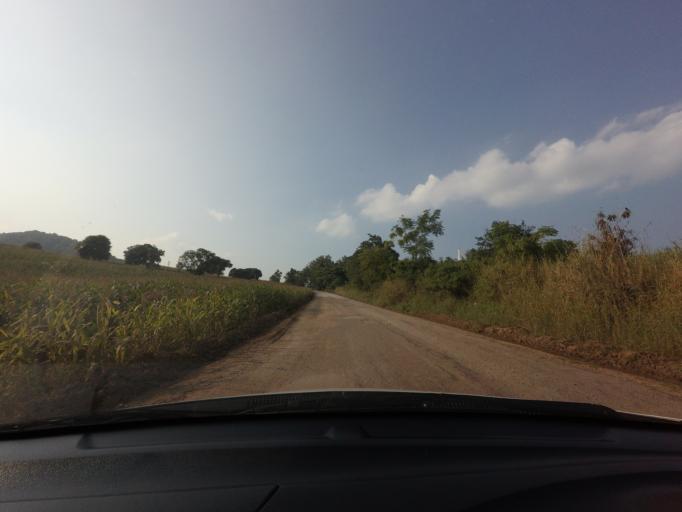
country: TH
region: Nakhon Ratchasima
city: Pak Chong
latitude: 14.5505
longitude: 101.5746
